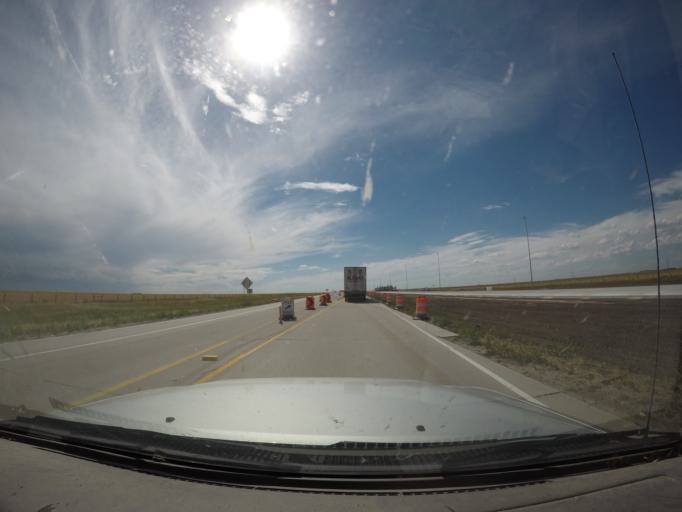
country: US
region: Colorado
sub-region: Sedgwick County
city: Julesburg
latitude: 41.0464
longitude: -102.3101
